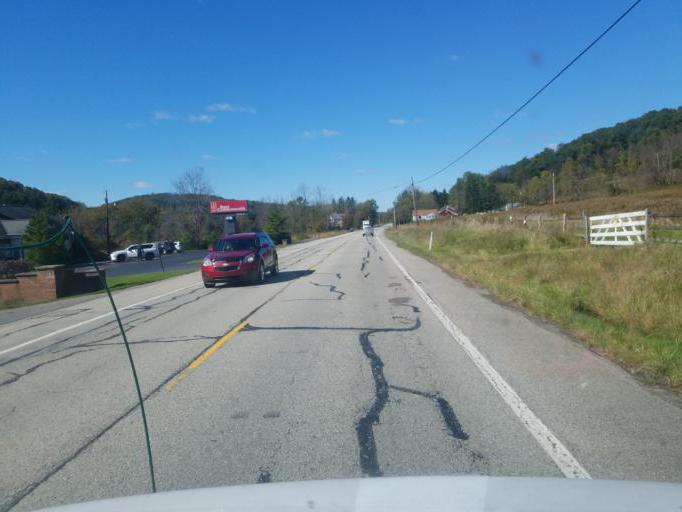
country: US
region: Pennsylvania
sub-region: Westmoreland County
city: Ligonier
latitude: 40.2170
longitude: -79.2078
